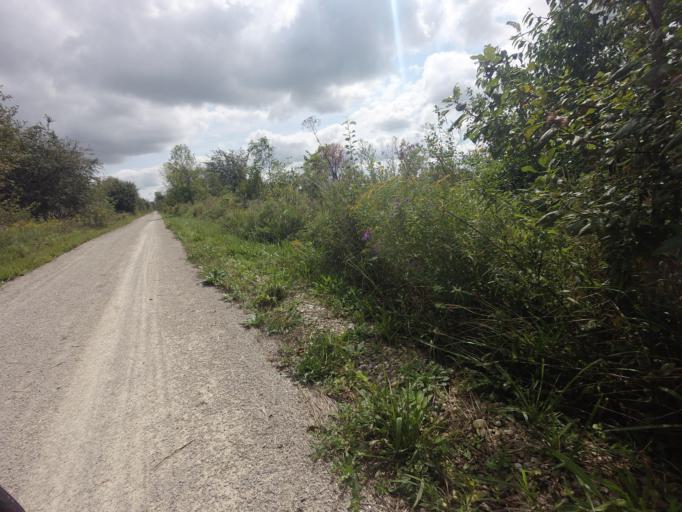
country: CA
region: Ontario
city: North Perth
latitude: 43.5821
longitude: -81.0623
